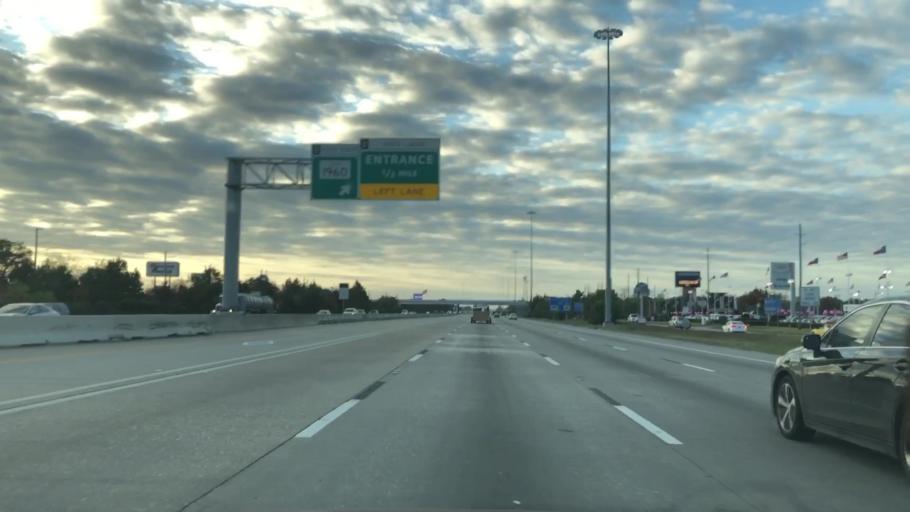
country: US
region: Texas
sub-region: Harris County
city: Spring
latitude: 30.0707
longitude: -95.4354
